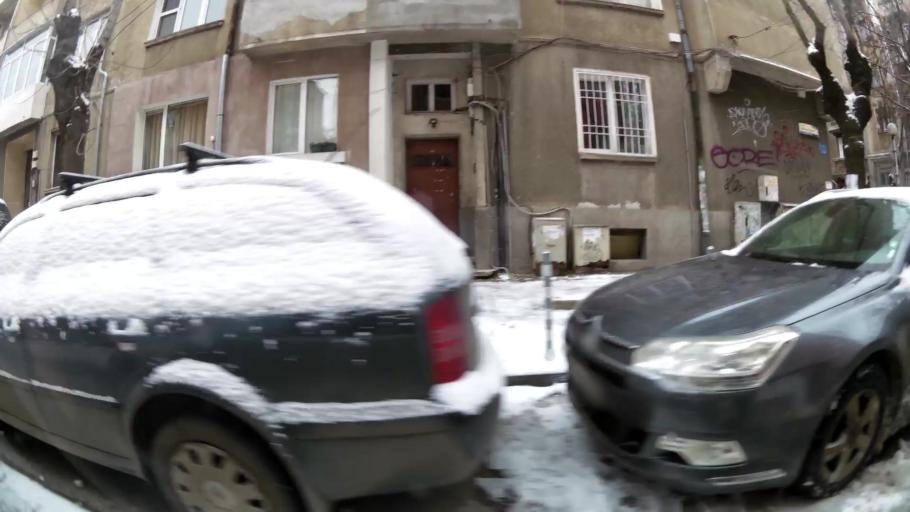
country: BG
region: Sofia-Capital
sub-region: Stolichna Obshtina
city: Sofia
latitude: 42.6938
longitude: 23.3505
